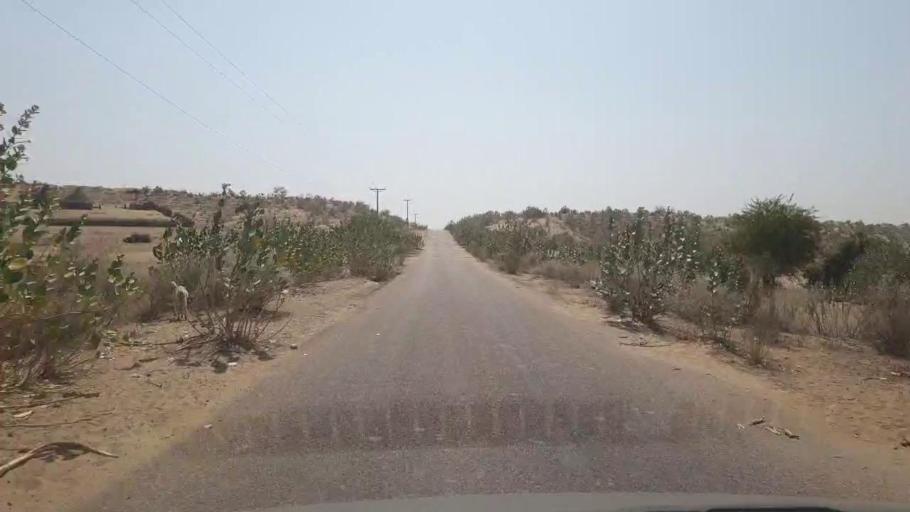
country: PK
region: Sindh
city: Chor
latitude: 25.6220
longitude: 70.1755
